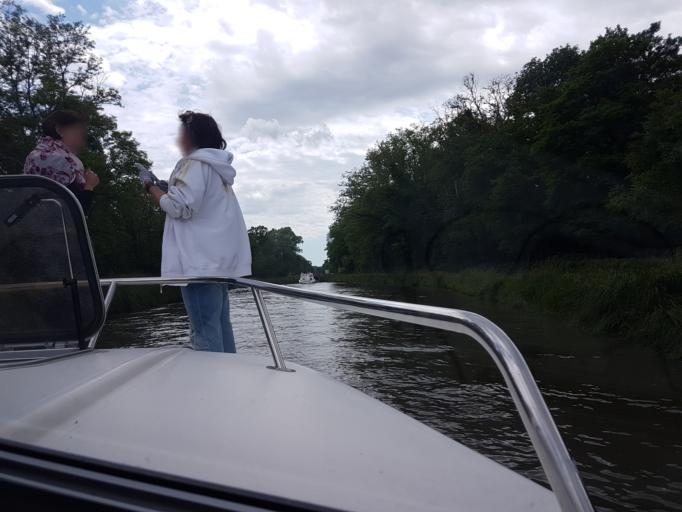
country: FR
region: Bourgogne
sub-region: Departement de la Nievre
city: Clamecy
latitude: 47.4894
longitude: 3.5244
